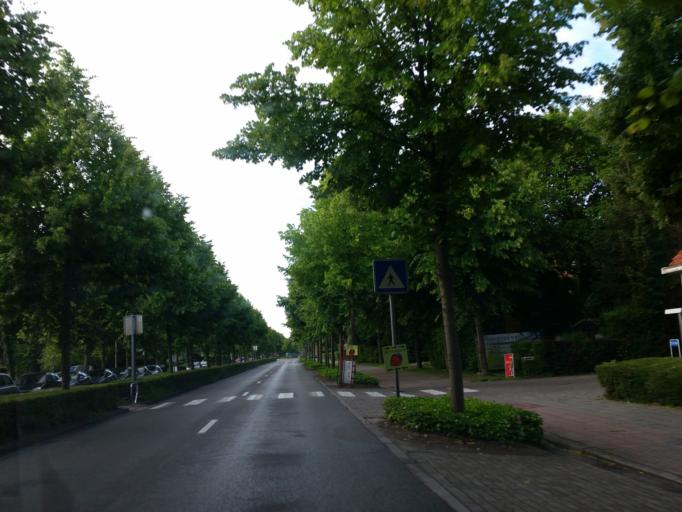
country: BE
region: Flanders
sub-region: Provincie Antwerpen
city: Brasschaat
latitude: 51.3028
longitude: 4.4861
